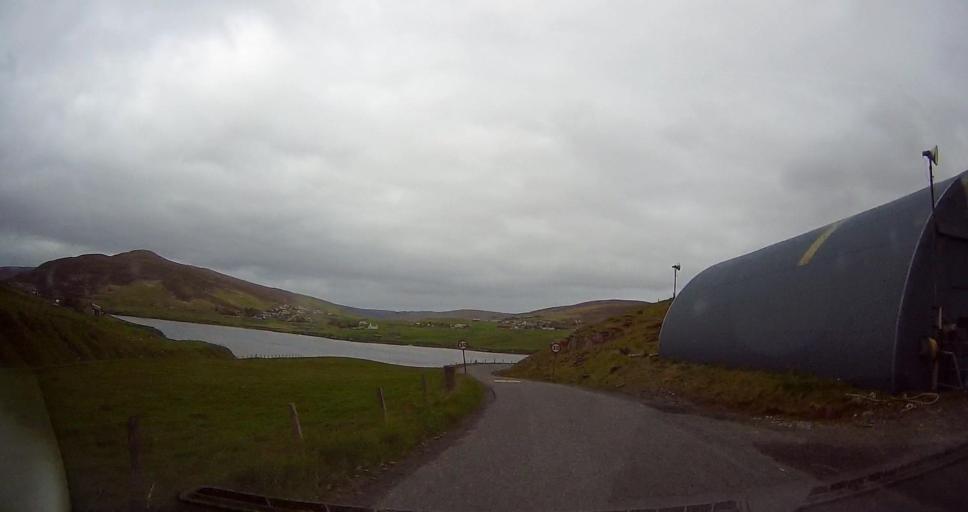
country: GB
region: Scotland
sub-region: Shetland Islands
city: Lerwick
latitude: 60.3464
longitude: -1.2713
